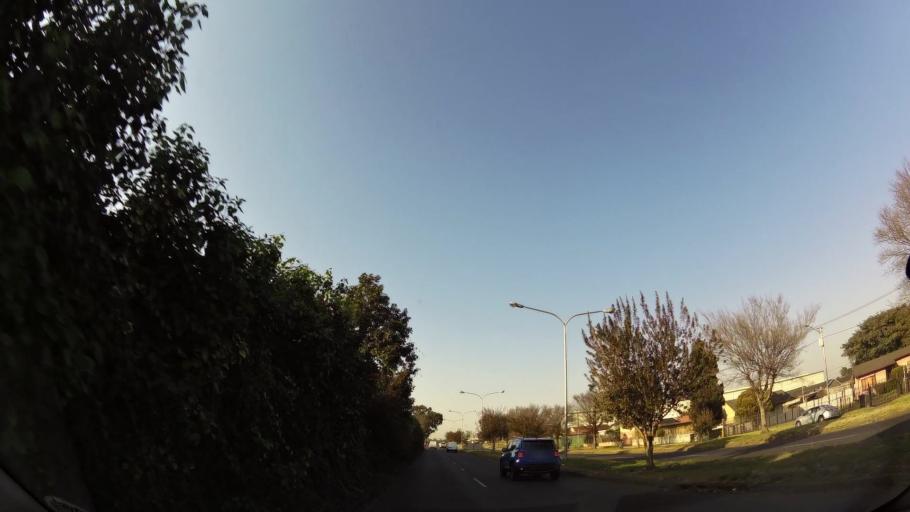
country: ZA
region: Gauteng
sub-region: City of Johannesburg Metropolitan Municipality
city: Modderfontein
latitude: -26.1494
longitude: 28.2013
